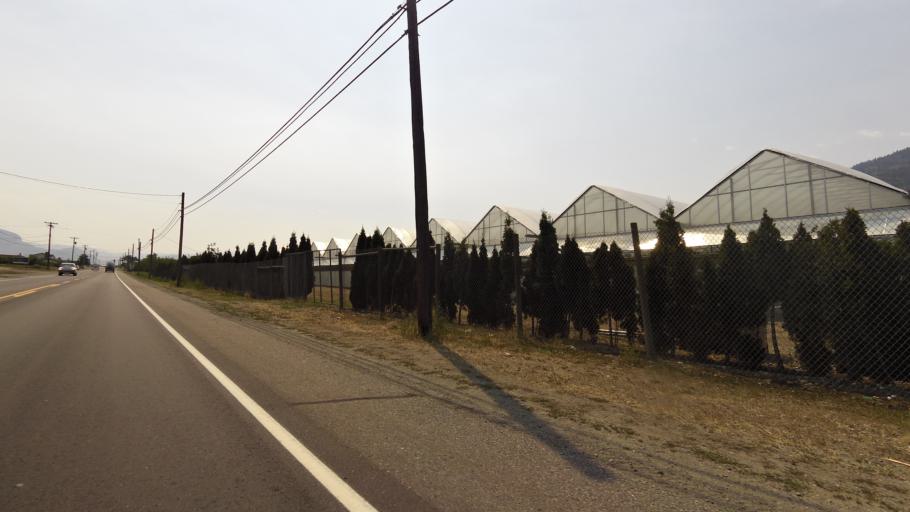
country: CA
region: British Columbia
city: Osoyoos
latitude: 49.0462
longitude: -119.4951
